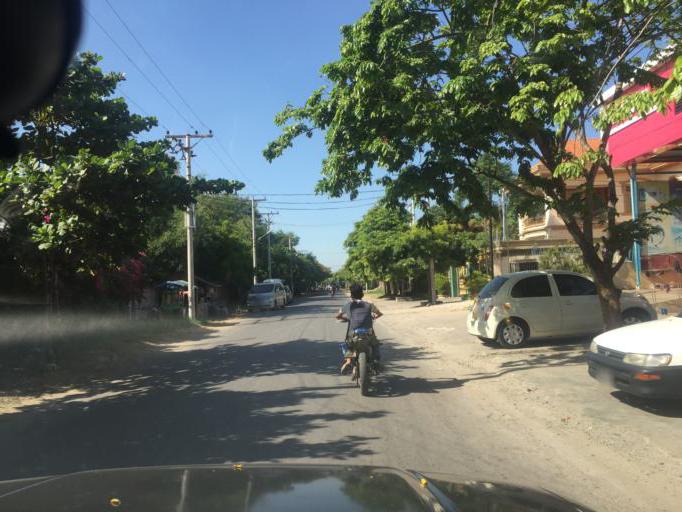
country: MM
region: Mandalay
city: Mandalay
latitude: 21.9532
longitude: 96.1098
